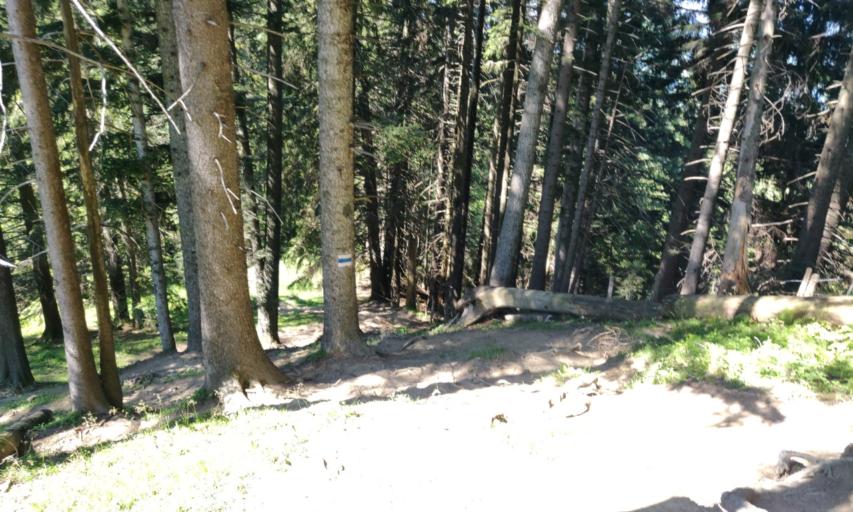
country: CH
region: Schwyz
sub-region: Bezirk Schwyz
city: Goldau
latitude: 47.0167
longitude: 8.5537
